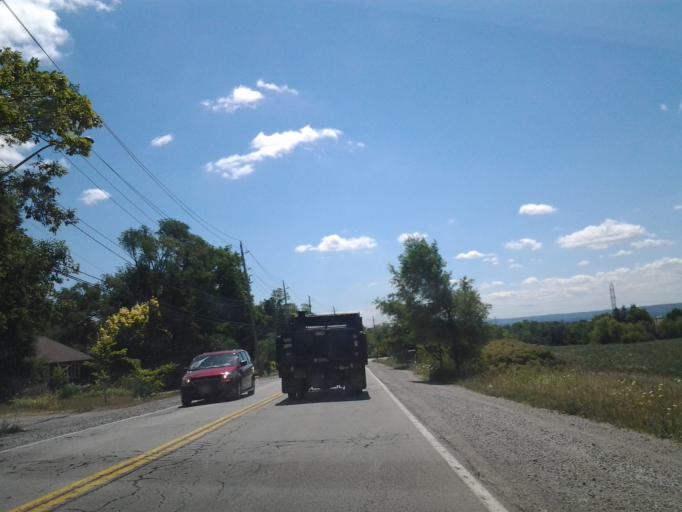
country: CA
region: Ontario
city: Hamilton
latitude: 43.3201
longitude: -79.8712
